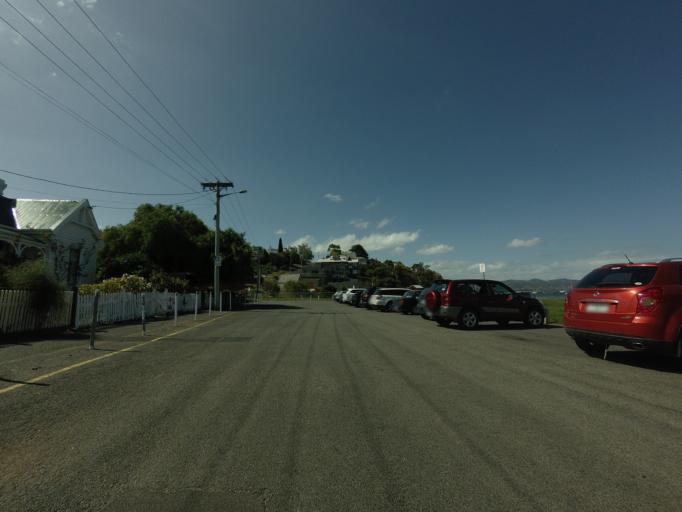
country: AU
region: Tasmania
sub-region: Hobart
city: Sandy Bay
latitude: -42.8949
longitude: 147.3332
